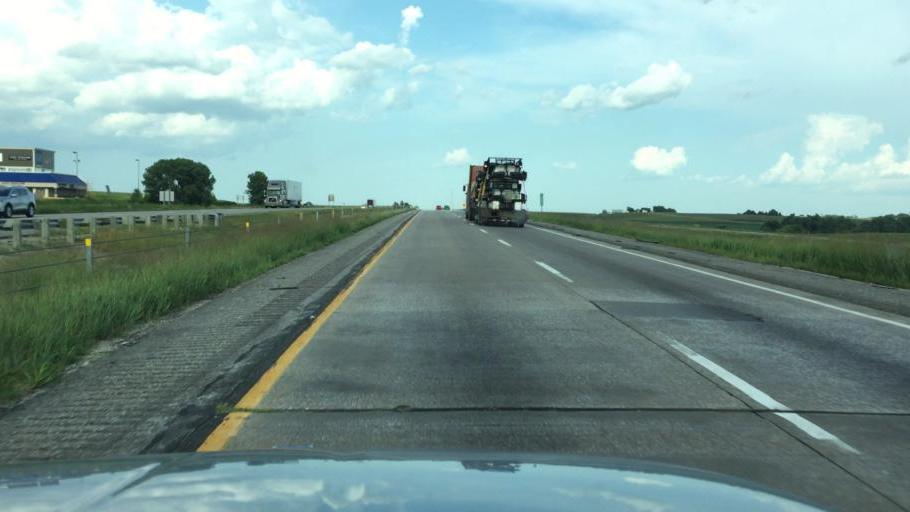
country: US
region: Iowa
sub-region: Iowa County
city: Williamsburg
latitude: 41.6870
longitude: -92.0074
